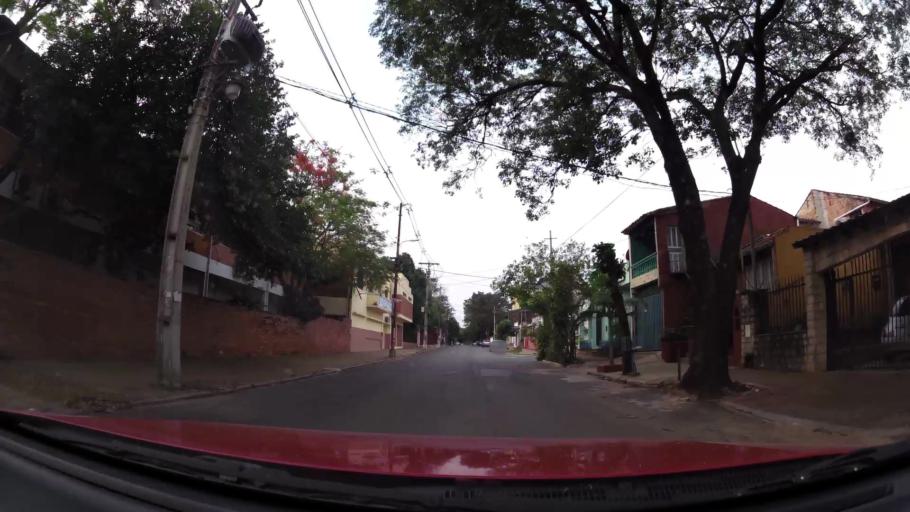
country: PY
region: Asuncion
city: Asuncion
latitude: -25.3069
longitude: -57.6104
